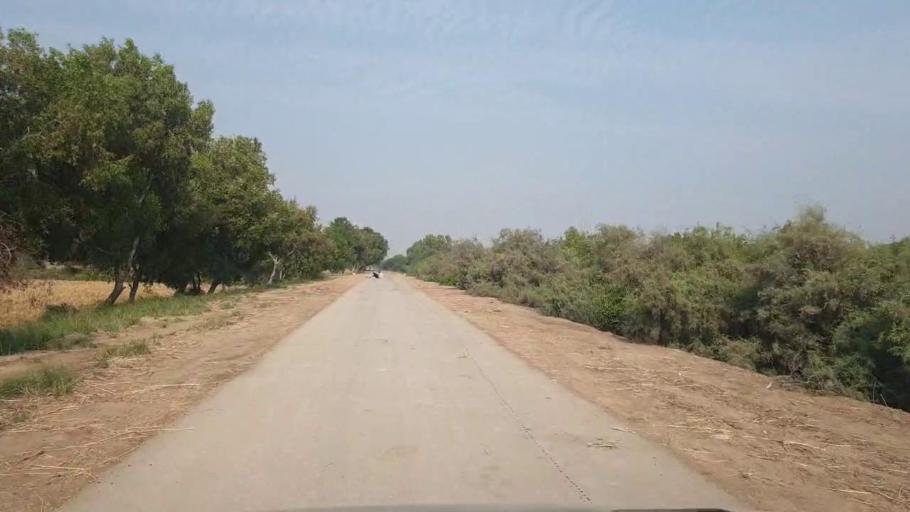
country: PK
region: Sindh
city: Tando Muhammad Khan
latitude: 25.1218
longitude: 68.4594
